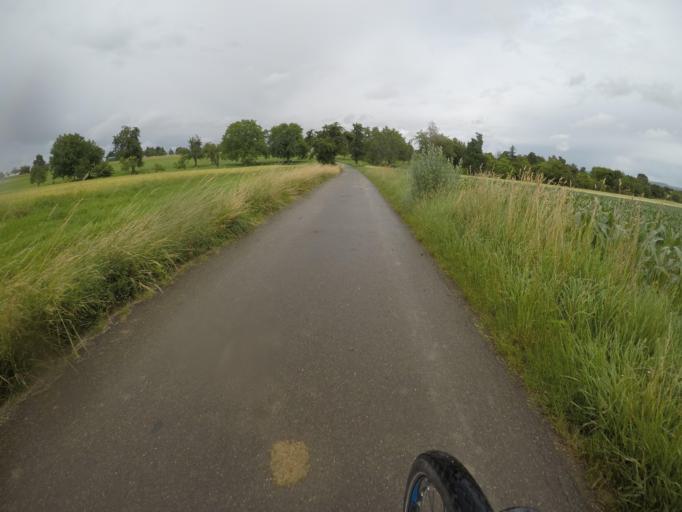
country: DE
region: Baden-Wuerttemberg
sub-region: Regierungsbezirk Stuttgart
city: Bondorf
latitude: 48.5557
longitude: 8.8281
